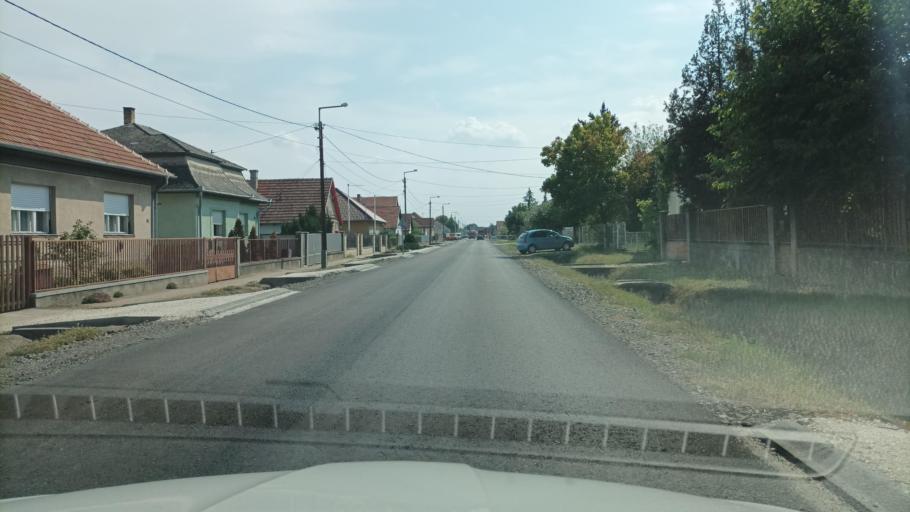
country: HU
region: Pest
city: Tura
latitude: 47.6006
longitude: 19.6025
